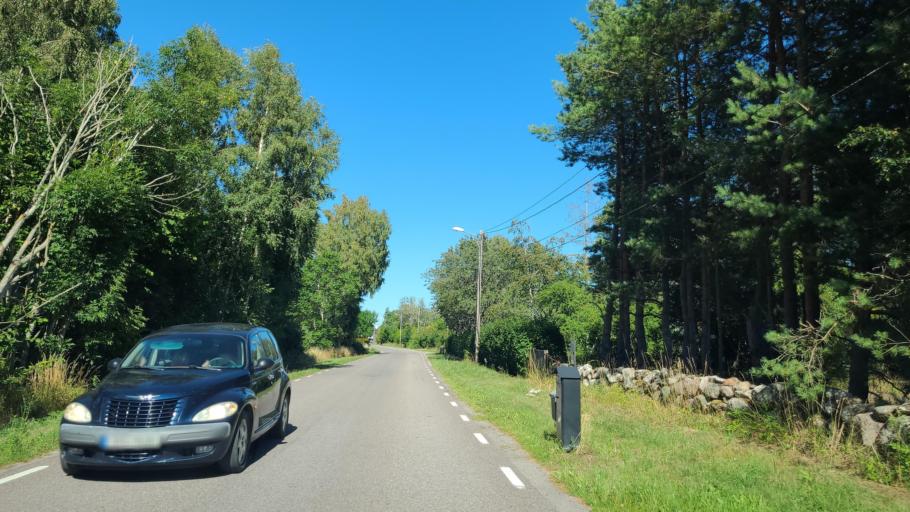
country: SE
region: Kalmar
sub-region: Borgholms Kommun
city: Borgholm
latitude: 56.8395
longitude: 16.7851
